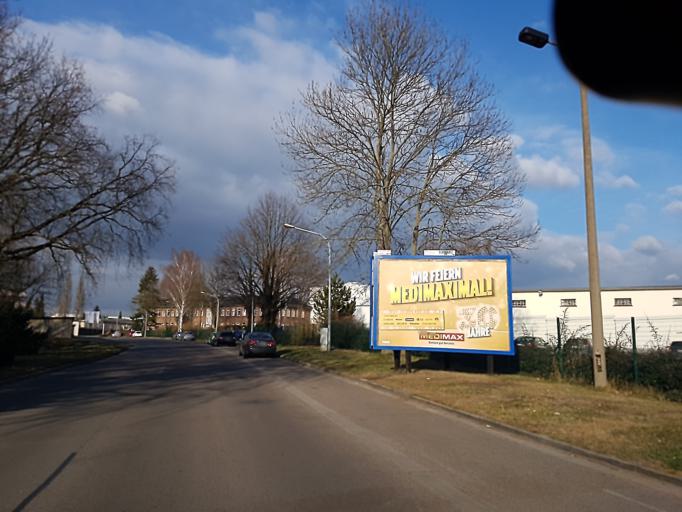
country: DE
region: Brandenburg
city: Finsterwalde
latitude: 51.6290
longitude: 13.7296
